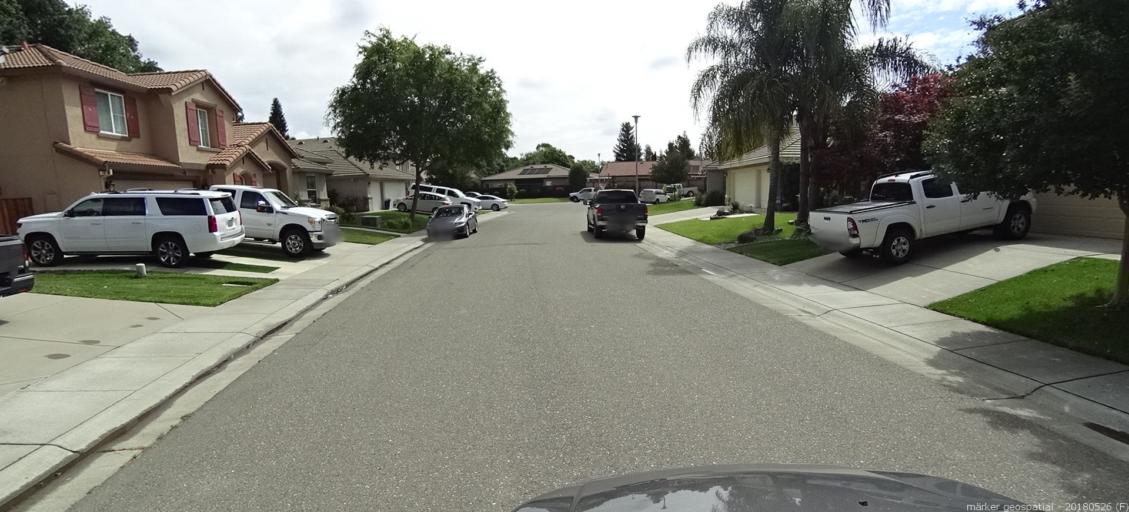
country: US
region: California
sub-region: Yolo County
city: West Sacramento
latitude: 38.6084
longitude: -121.5356
